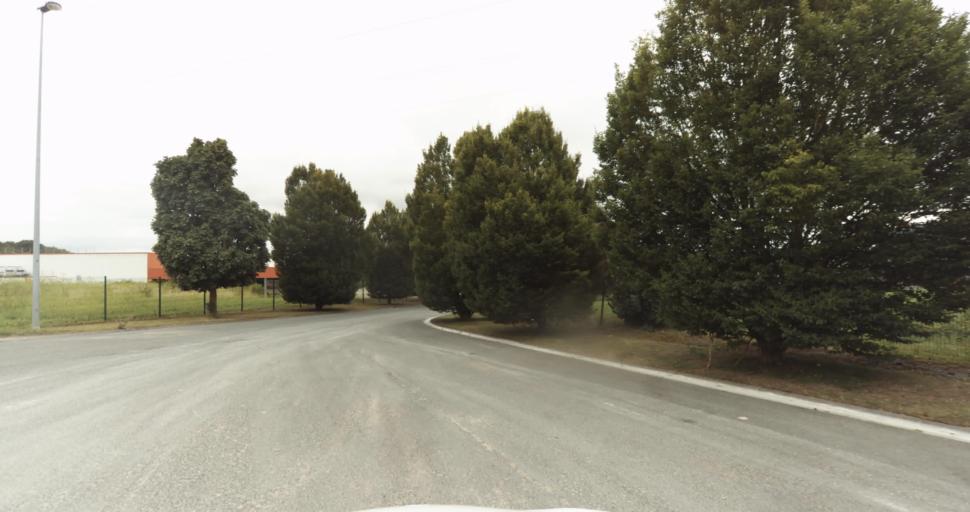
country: FR
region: Haute-Normandie
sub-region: Departement de l'Eure
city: Gravigny
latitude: 49.0351
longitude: 1.1809
